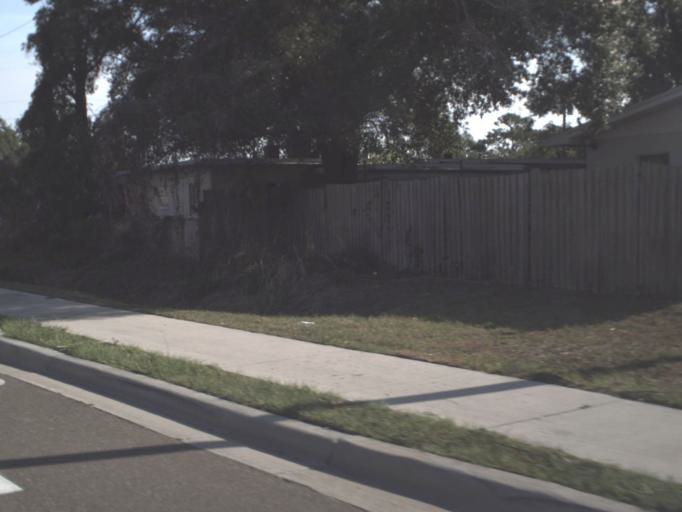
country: US
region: Florida
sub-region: Orange County
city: Fairview Shores
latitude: 28.6027
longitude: -81.4176
